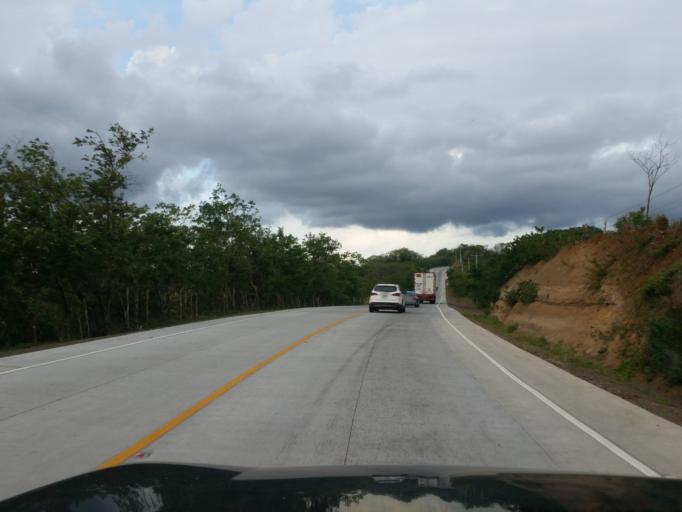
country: NI
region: Managua
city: Ciudad Sandino
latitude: 12.0800
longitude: -86.4213
